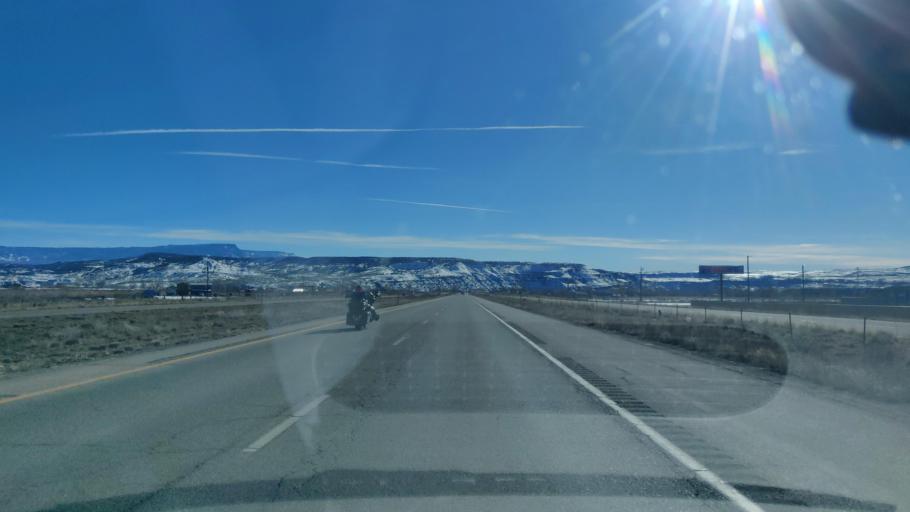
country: US
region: Colorado
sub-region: Garfield County
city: Parachute
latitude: 39.3020
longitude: -108.2194
